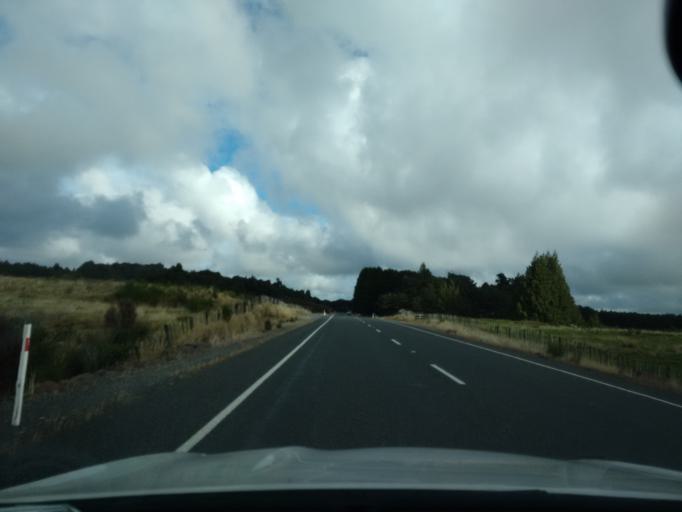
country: NZ
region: Manawatu-Wanganui
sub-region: Ruapehu District
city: Waiouru
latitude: -39.2953
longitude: 175.3878
